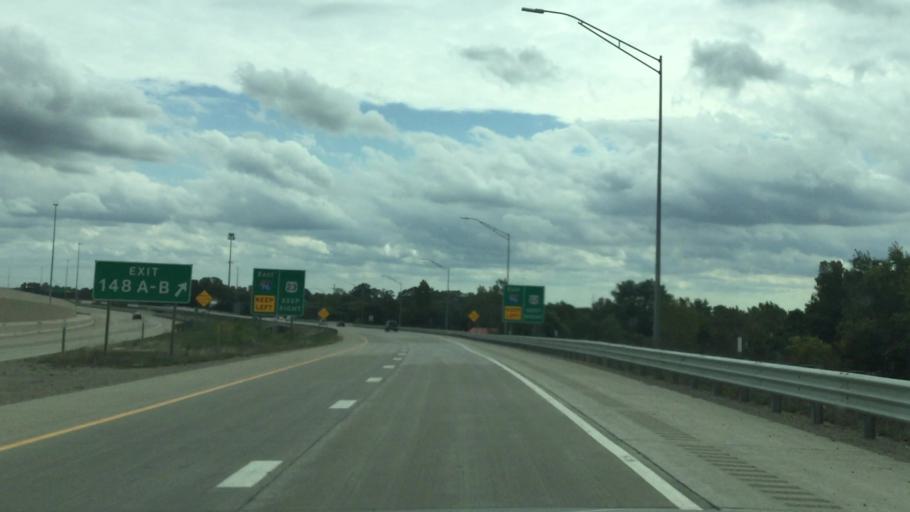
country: US
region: Michigan
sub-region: Livingston County
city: Brighton
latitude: 42.5268
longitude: -83.7622
